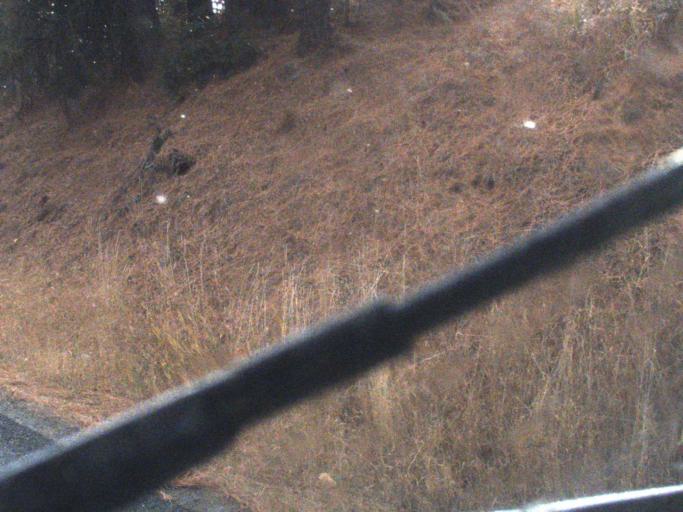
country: US
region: Washington
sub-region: Stevens County
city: Kettle Falls
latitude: 48.4240
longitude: -118.1696
